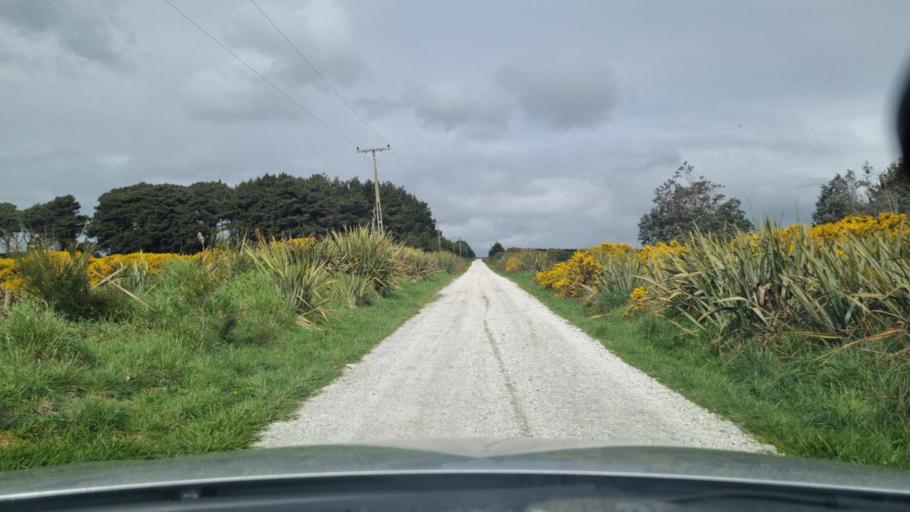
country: NZ
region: Southland
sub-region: Invercargill City
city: Bluff
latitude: -46.5115
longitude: 168.3519
